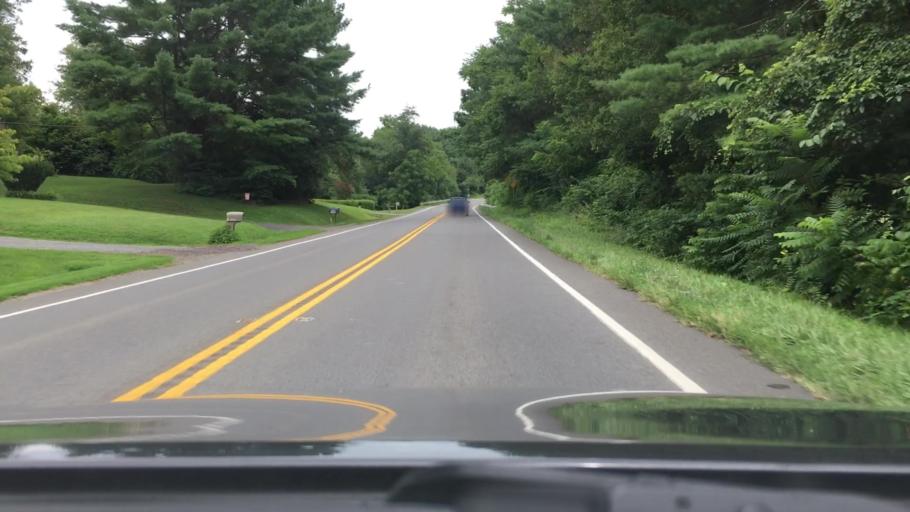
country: US
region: Virginia
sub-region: Orange County
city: Orange
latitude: 38.2448
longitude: -78.0854
